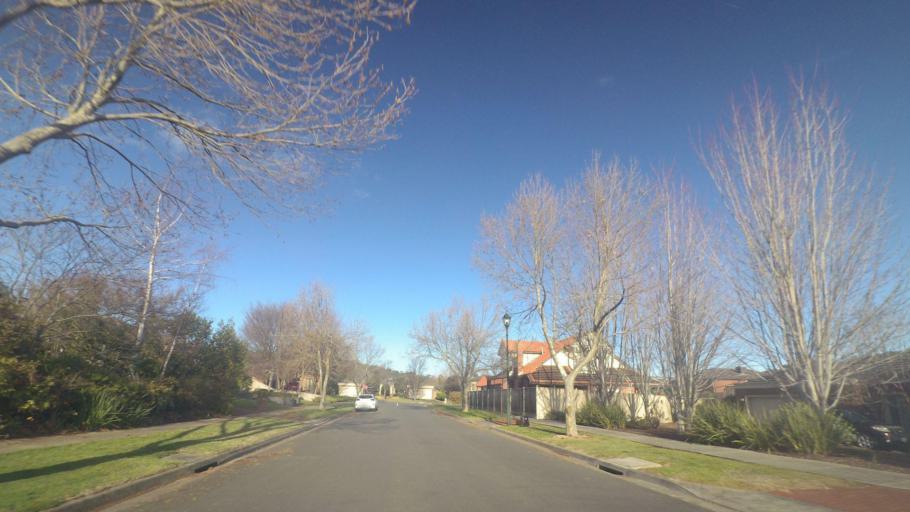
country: AU
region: Victoria
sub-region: Yarra Ranges
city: Lysterfield
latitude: -37.9159
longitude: 145.2873
